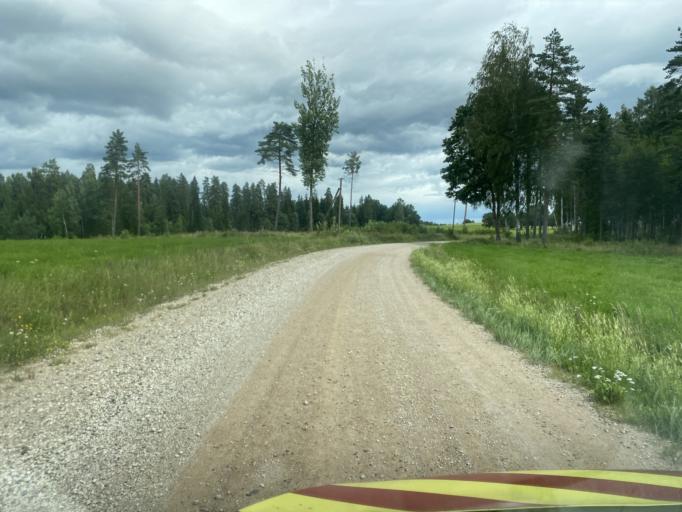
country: EE
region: Valgamaa
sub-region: Torva linn
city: Torva
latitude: 57.9493
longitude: 25.9401
